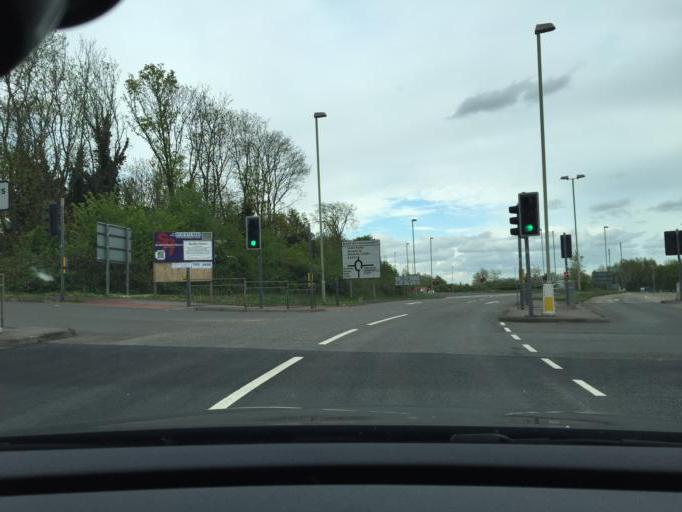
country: GB
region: England
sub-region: Wokingham
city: Shinfield
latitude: 51.4160
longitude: -0.9516
